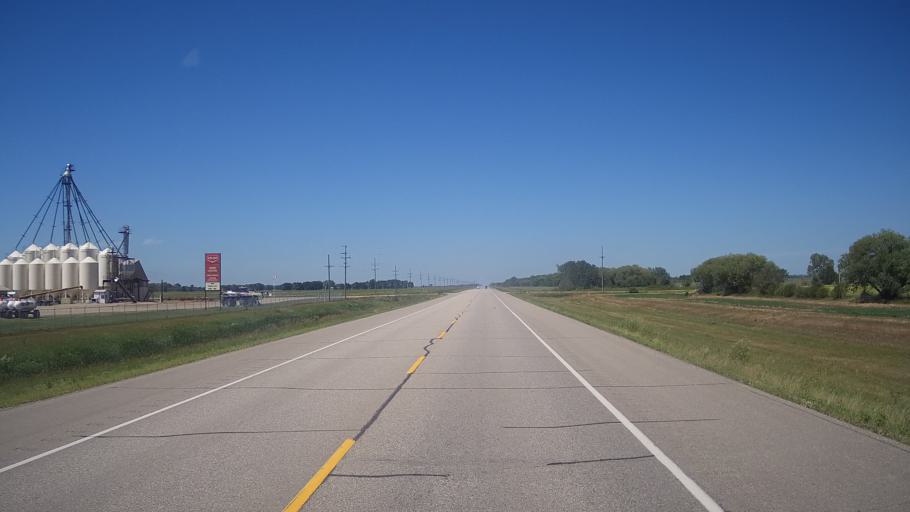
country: CA
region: Manitoba
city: Neepawa
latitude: 50.2257
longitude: -99.0392
